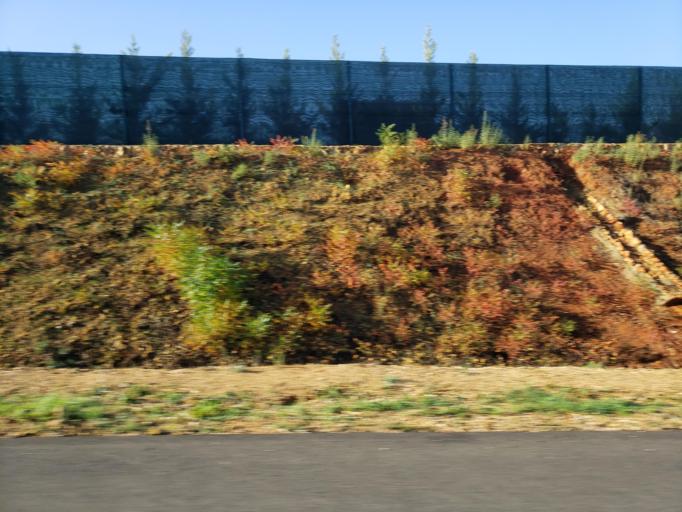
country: PT
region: Faro
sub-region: Portimao
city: Alvor
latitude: 37.1574
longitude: -8.5703
